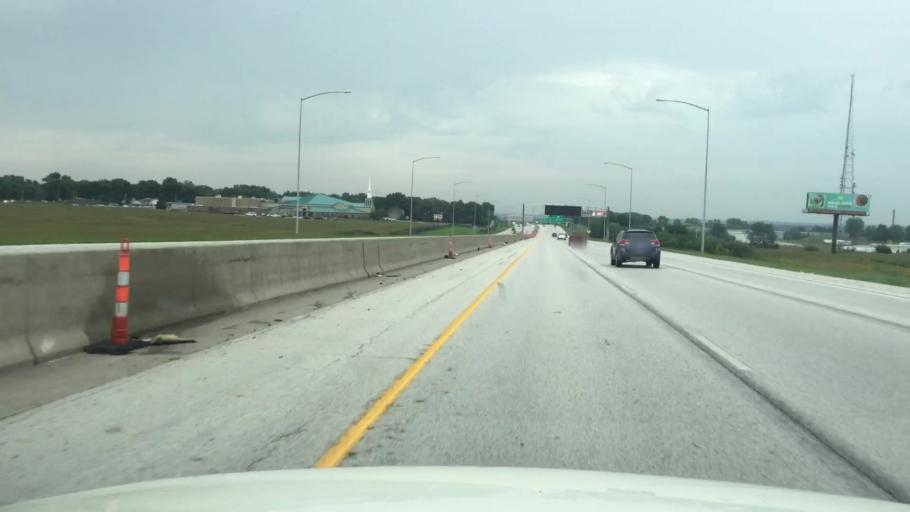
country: US
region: Iowa
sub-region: Polk County
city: Des Moines
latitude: 41.6429
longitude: -93.5758
